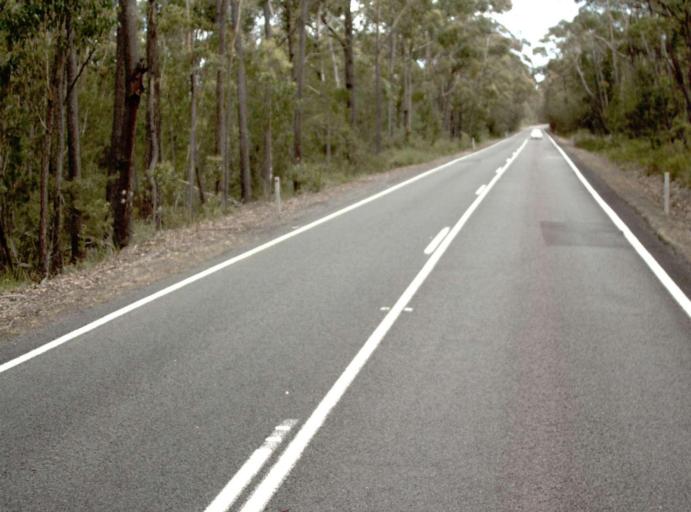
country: AU
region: New South Wales
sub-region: Bega Valley
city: Eden
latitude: -37.4938
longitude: 149.5496
